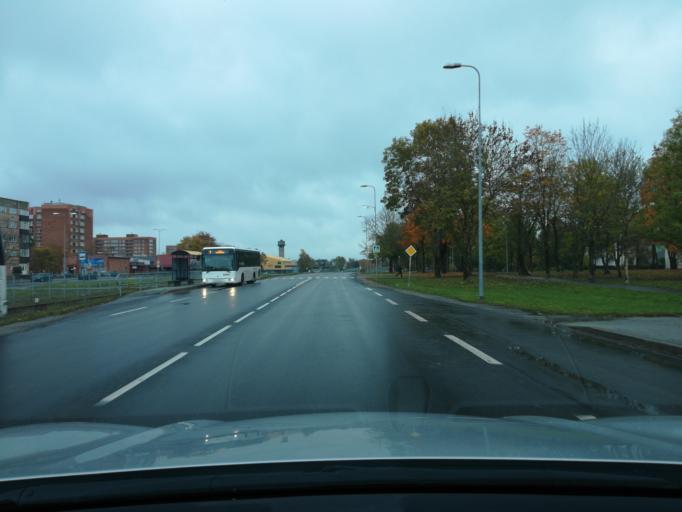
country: EE
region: Ida-Virumaa
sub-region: Johvi vald
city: Johvi
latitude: 59.3291
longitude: 27.4155
